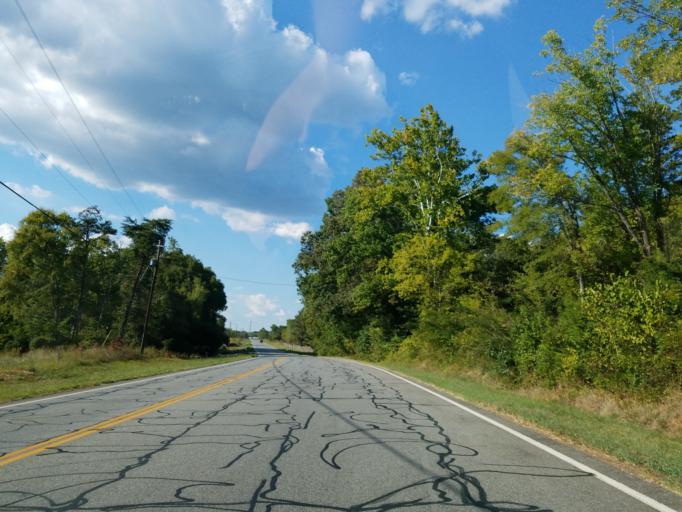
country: US
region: Georgia
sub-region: Bartow County
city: Rydal
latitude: 34.4879
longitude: -84.7064
